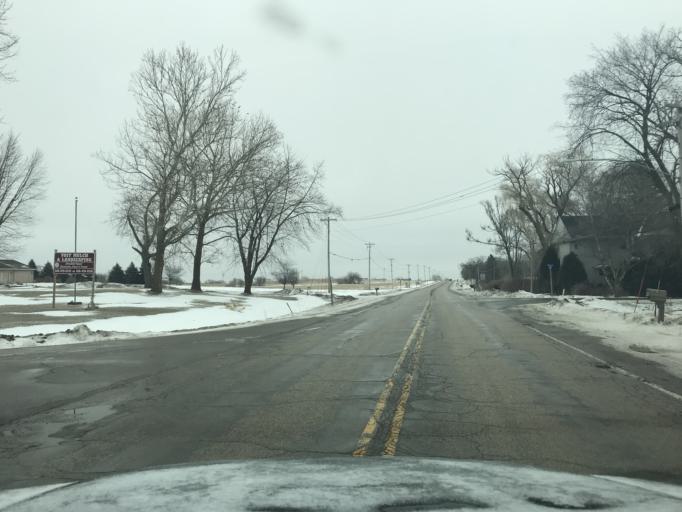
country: US
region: Wisconsin
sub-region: Dane County
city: Cottage Grove
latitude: 43.0897
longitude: -89.2353
